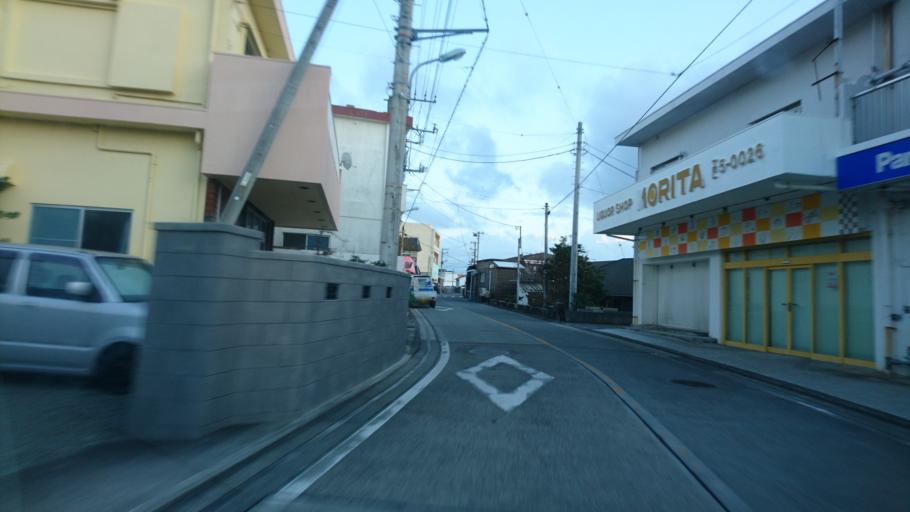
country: JP
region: Shizuoka
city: Shimoda
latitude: 34.3744
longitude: 139.2555
